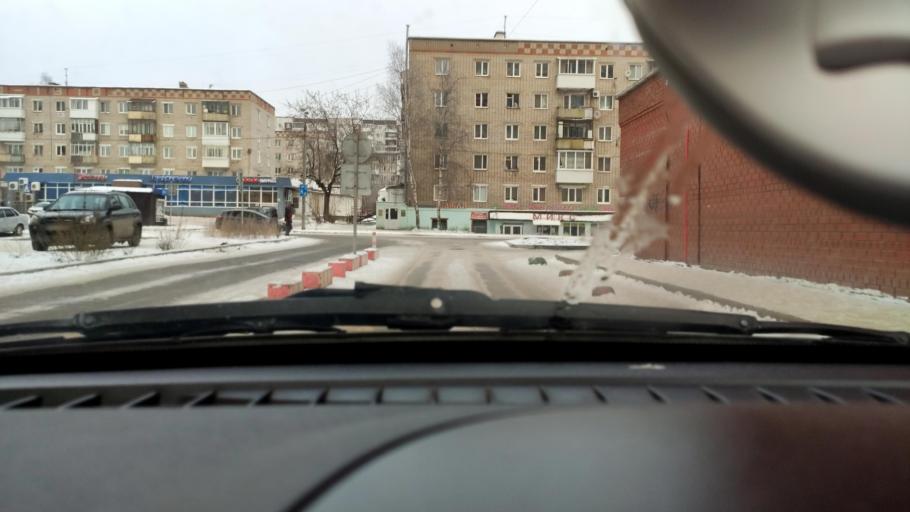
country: RU
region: Perm
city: Perm
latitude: 58.0843
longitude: 56.4044
